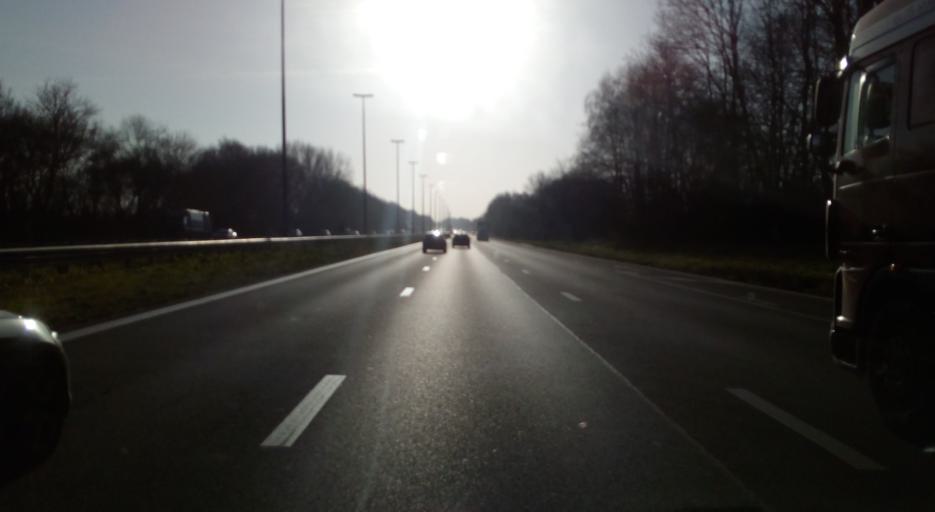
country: BE
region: Wallonia
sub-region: Province du Brabant Wallon
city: Braine-le-Chateau
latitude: 50.6539
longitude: 4.3096
